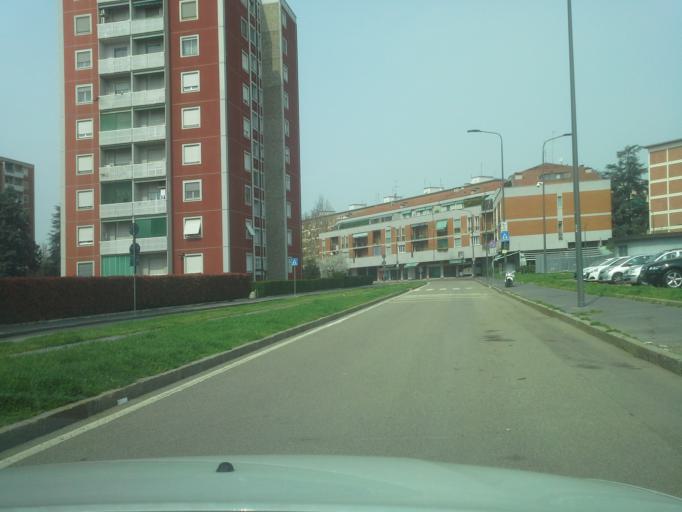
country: IT
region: Lombardy
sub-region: Citta metropolitana di Milano
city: Cesano Boscone
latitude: 45.4531
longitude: 9.0801
